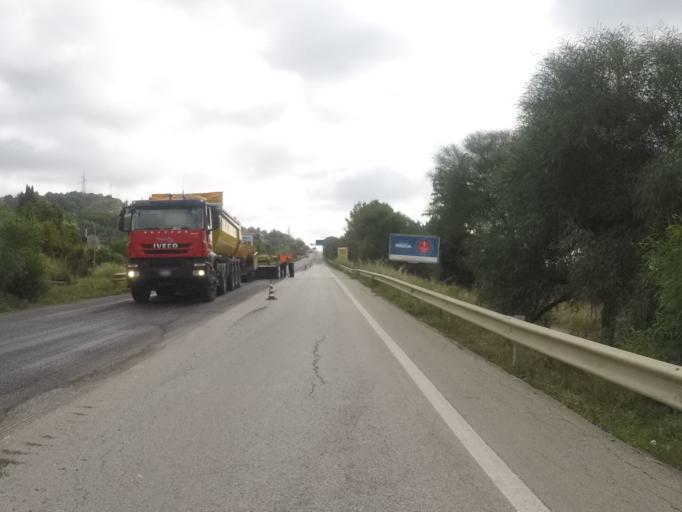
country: IT
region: Sicily
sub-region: Provincia di Caltanissetta
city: Caltanissetta
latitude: 37.4738
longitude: 14.0199
